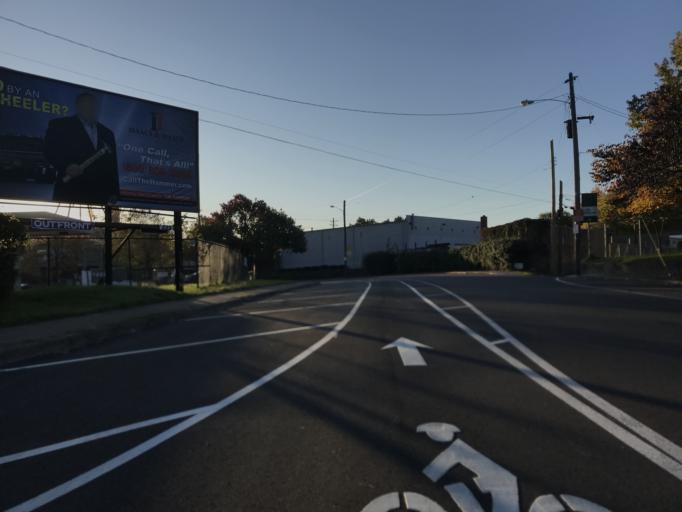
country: US
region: Kentucky
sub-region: Jefferson County
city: Louisville
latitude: 38.2367
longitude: -85.7403
